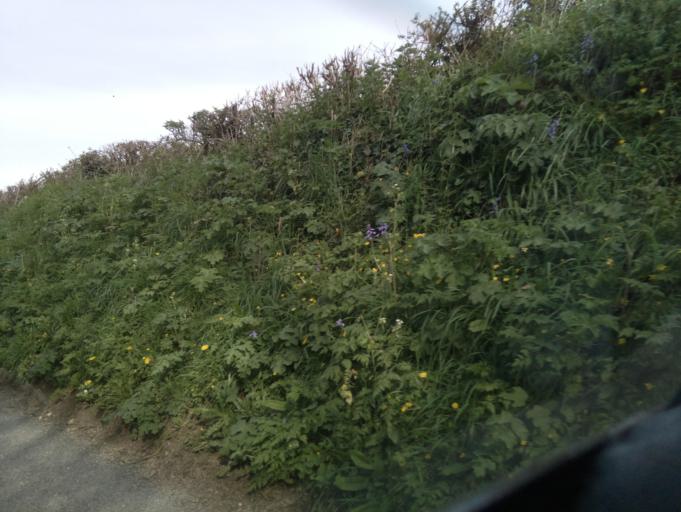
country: GB
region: England
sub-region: Dorset
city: Sherborne
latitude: 50.9371
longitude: -2.5155
